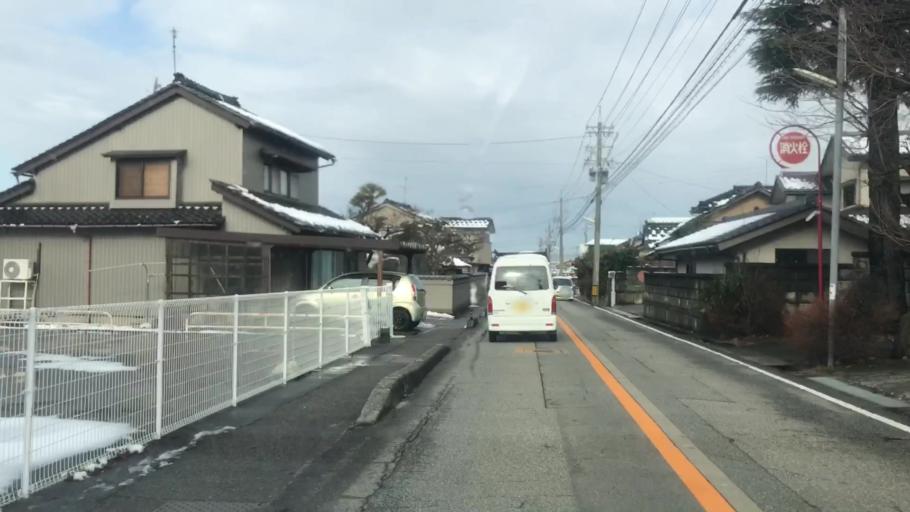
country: JP
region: Toyama
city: Toyama-shi
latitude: 36.6317
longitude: 137.2466
